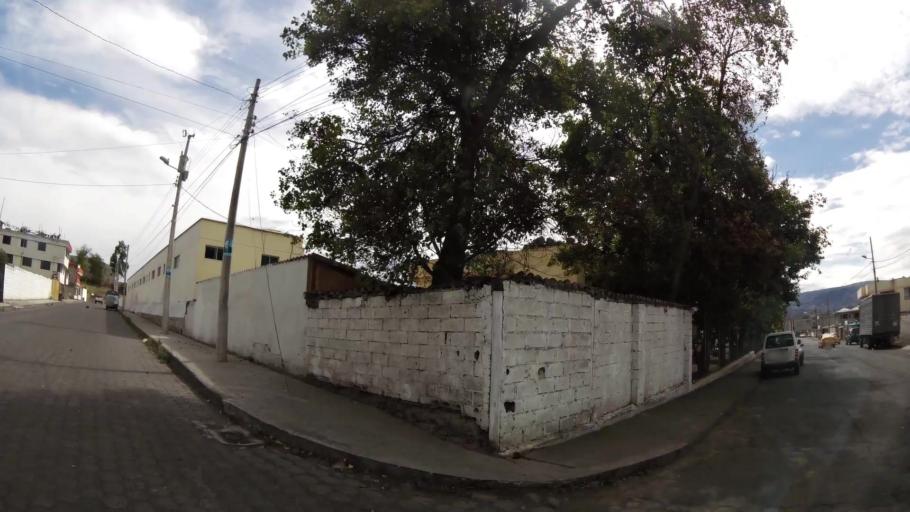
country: EC
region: Cotopaxi
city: Latacunga
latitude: -0.9257
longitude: -78.6037
